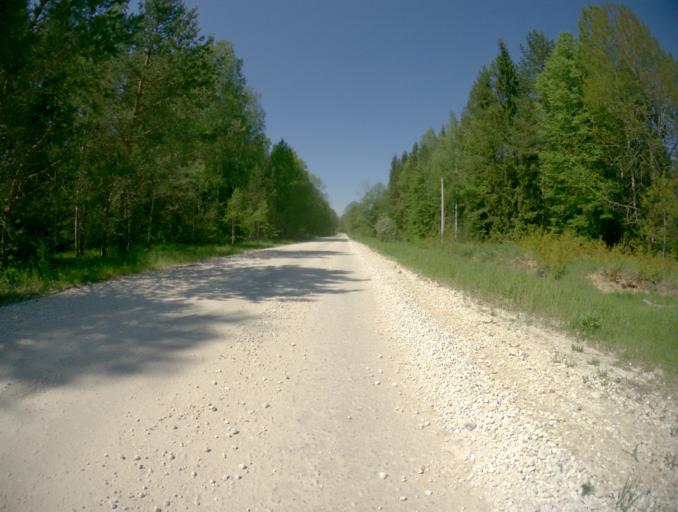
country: RU
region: Vladimir
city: Anopino
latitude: 55.7090
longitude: 40.6373
